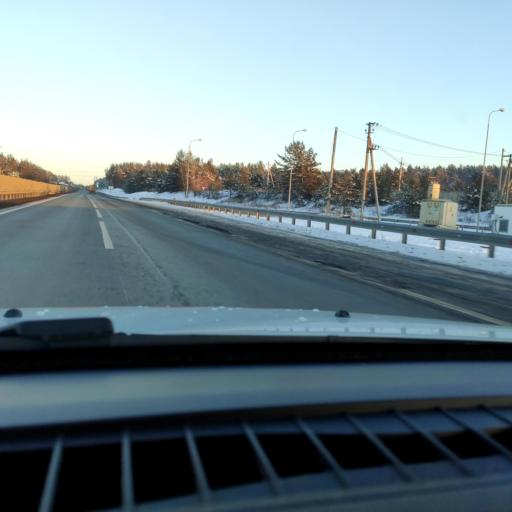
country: RU
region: Samara
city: Kurumoch
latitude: 53.4960
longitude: 50.0622
